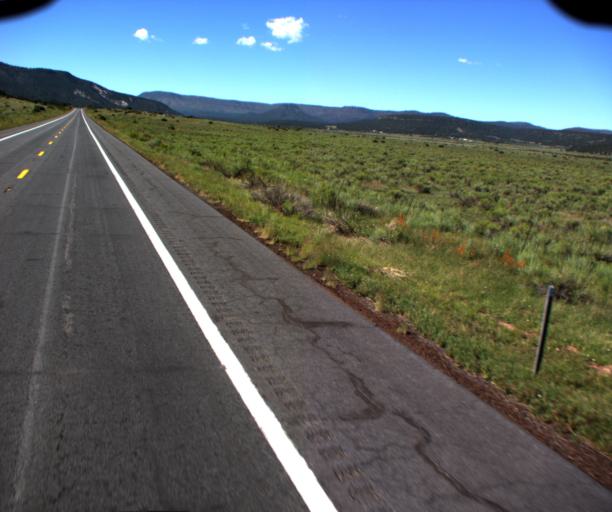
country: US
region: Arizona
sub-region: Apache County
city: Eagar
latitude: 34.0119
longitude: -109.1863
